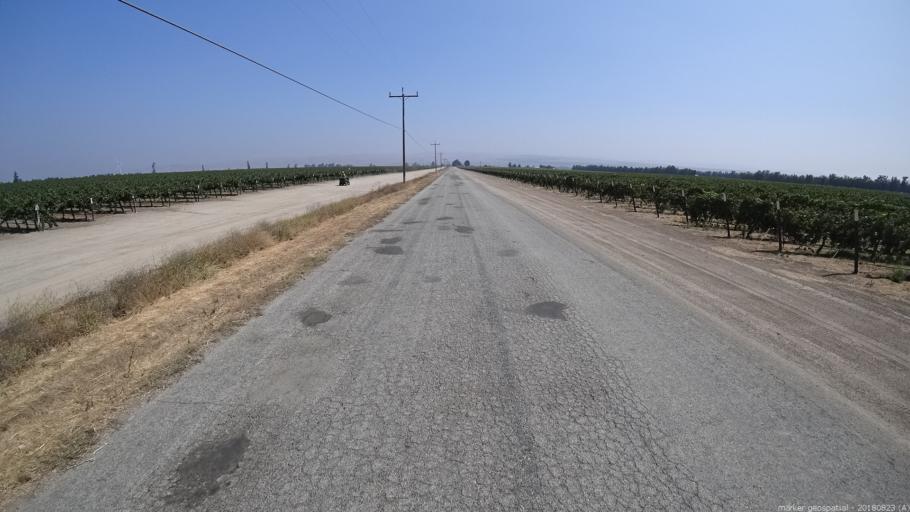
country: US
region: California
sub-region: Monterey County
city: King City
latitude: 36.2529
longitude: -121.1958
